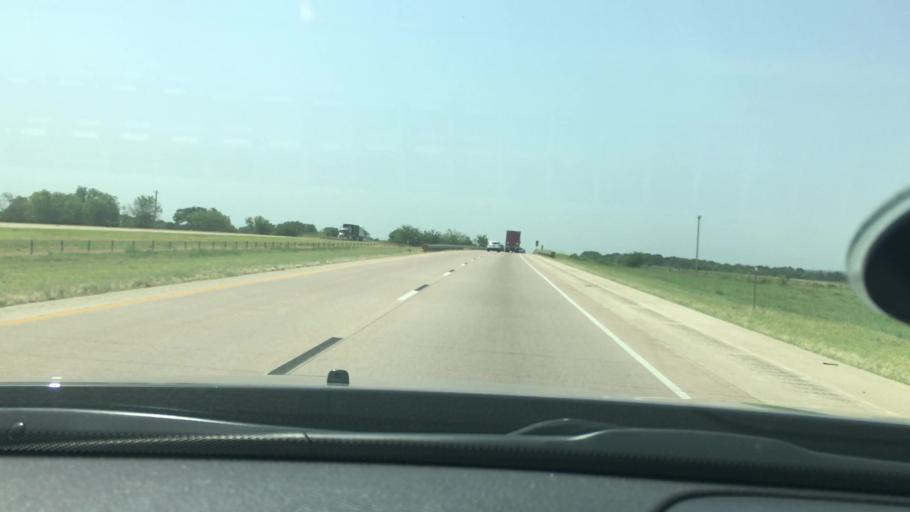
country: US
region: Oklahoma
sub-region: Garvin County
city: Pauls Valley
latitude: 34.6831
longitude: -97.2290
